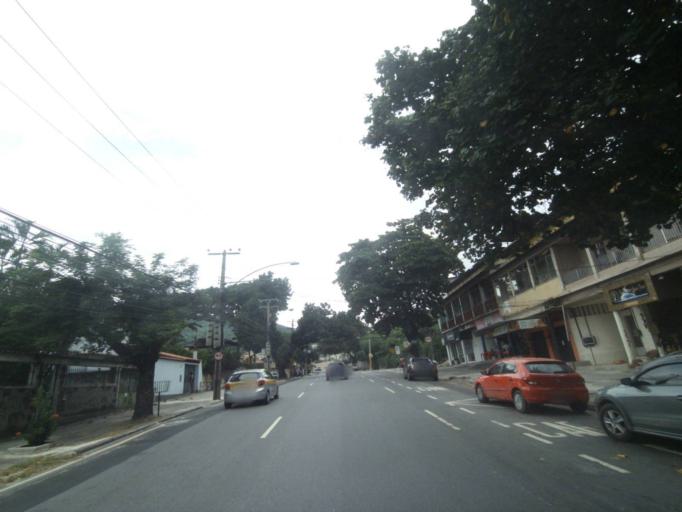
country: BR
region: Rio de Janeiro
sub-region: Nilopolis
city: Nilopolis
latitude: -22.8876
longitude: -43.3943
